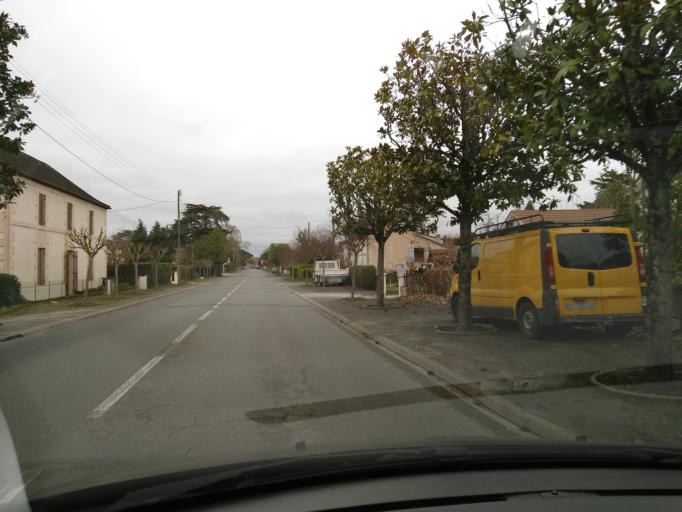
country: FR
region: Aquitaine
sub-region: Departement de la Dordogne
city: Bergerac
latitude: 44.8404
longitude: 0.4875
